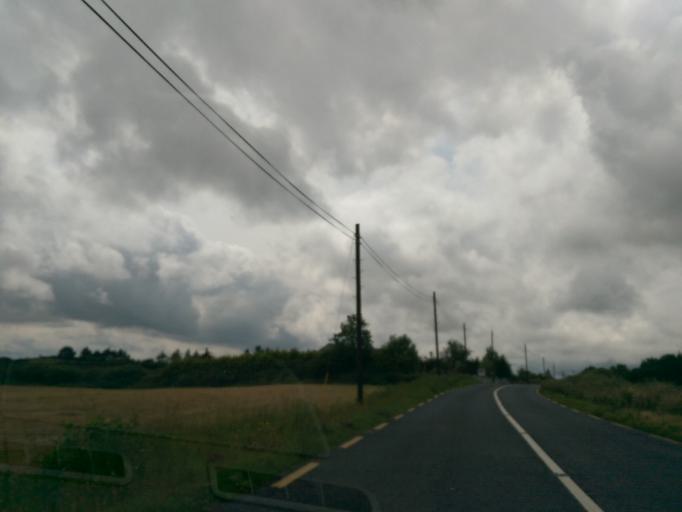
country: IE
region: Munster
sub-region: An Clar
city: Ennis
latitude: 52.7750
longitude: -9.0857
